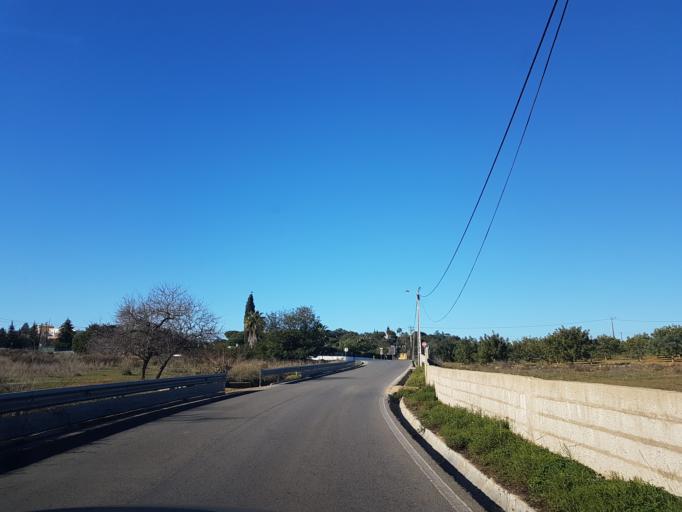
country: PT
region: Faro
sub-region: Lagoa
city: Lagoa
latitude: 37.1180
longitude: -8.4163
